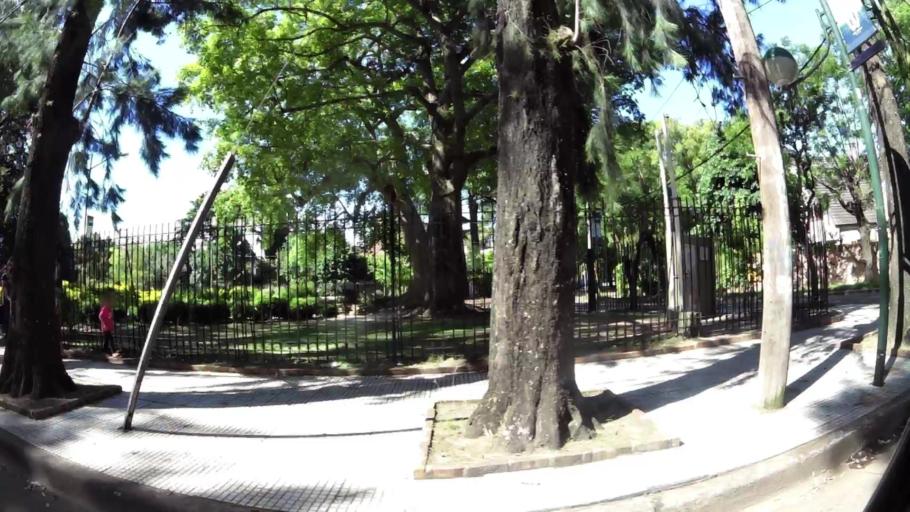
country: AR
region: Buenos Aires
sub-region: Partido de San Isidro
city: San Isidro
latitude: -34.4586
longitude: -58.5291
